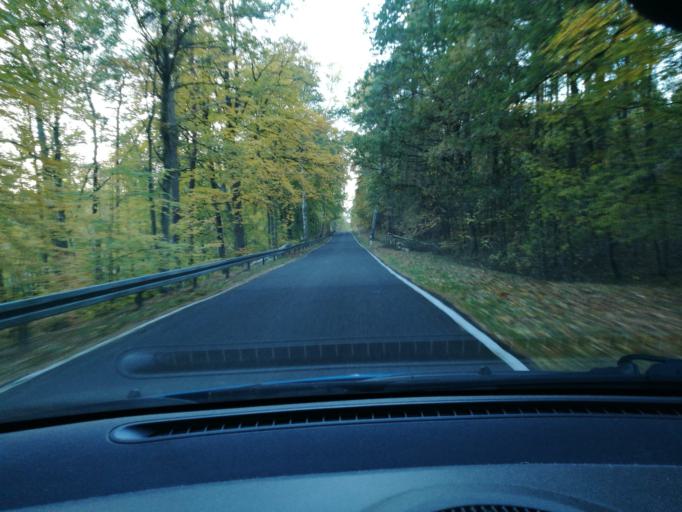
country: DE
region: Brandenburg
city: Karstadt
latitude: 53.0927
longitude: 11.7289
